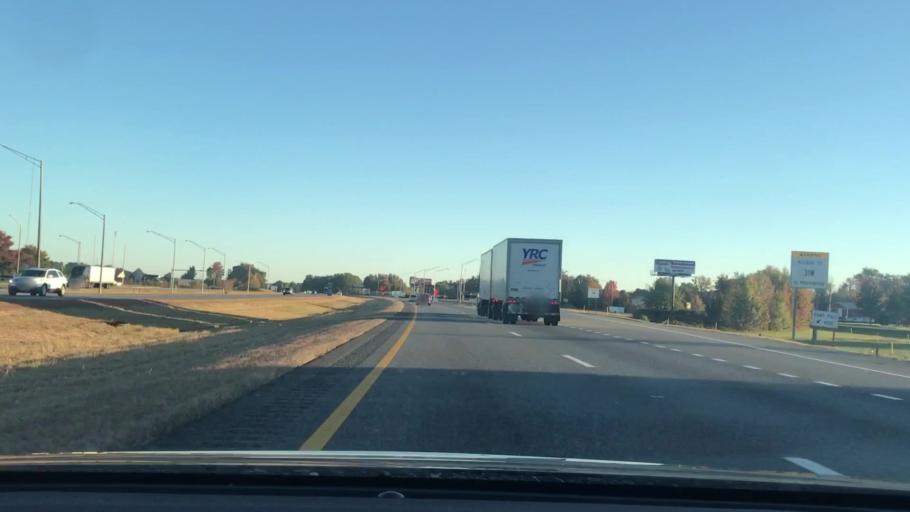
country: US
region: Tennessee
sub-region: Sumner County
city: Portland
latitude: 36.6071
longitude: -86.5822
